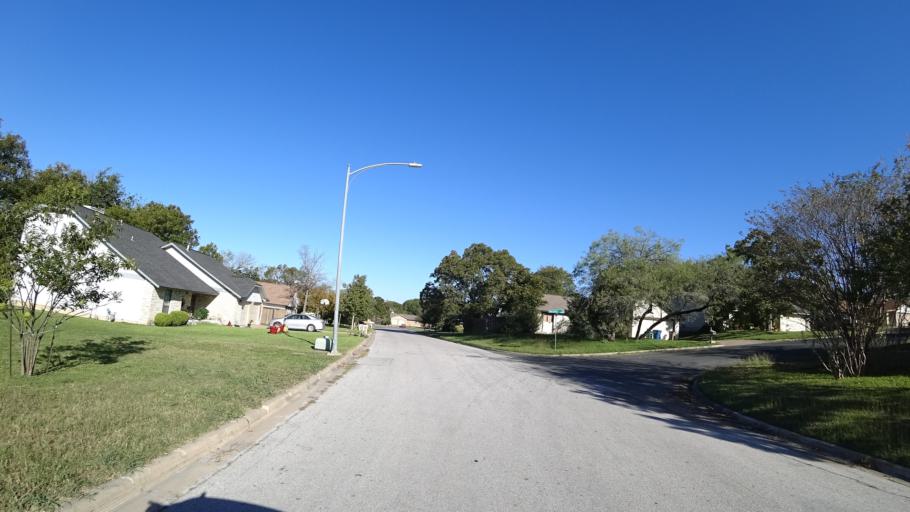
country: US
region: Texas
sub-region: Travis County
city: Austin
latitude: 30.3047
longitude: -97.6666
